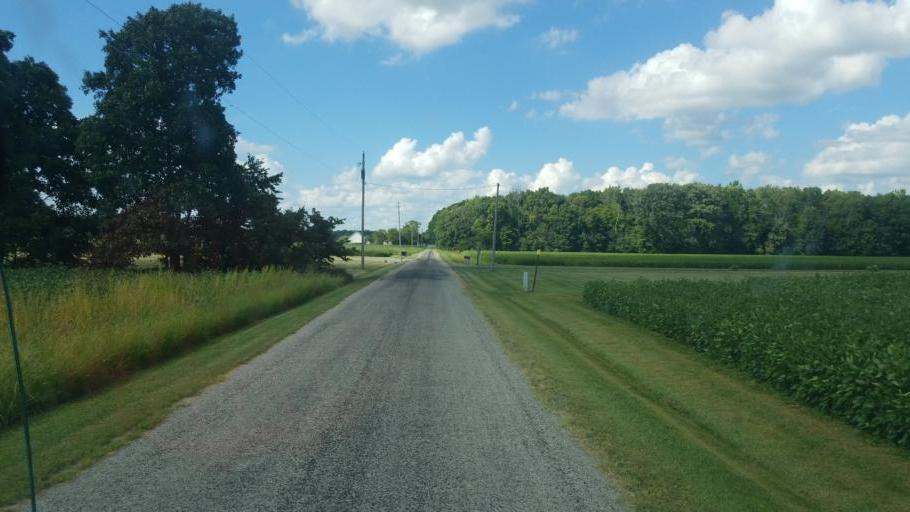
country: US
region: Ohio
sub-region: Union County
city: Richwood
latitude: 40.4601
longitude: -83.3425
